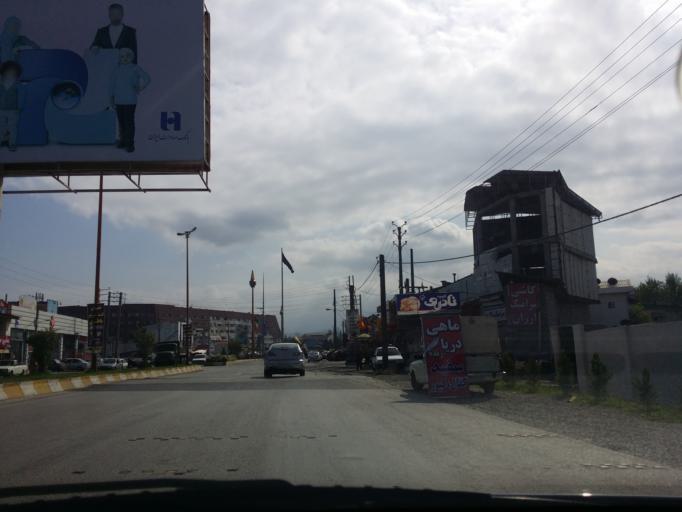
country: IR
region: Mazandaran
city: Chalus
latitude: 36.6834
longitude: 51.4009
